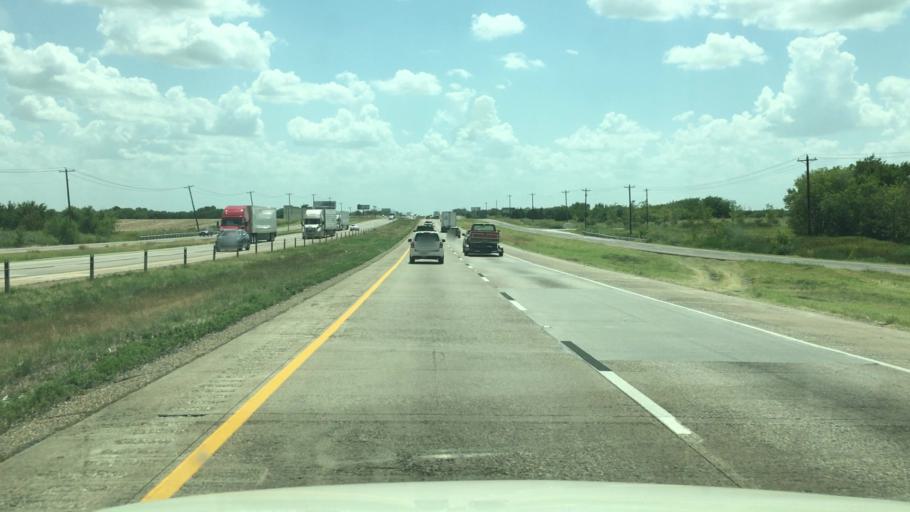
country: US
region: Texas
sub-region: Rockwall County
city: Fate
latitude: 32.9547
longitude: -96.3557
